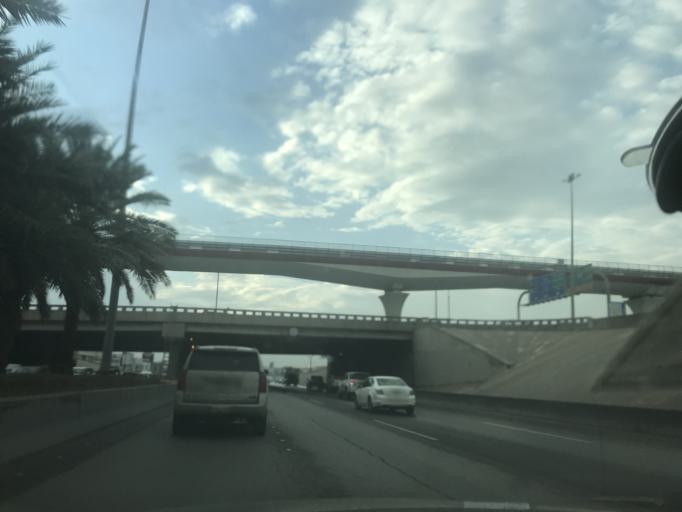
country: SA
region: Ar Riyad
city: Riyadh
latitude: 24.7608
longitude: 46.7386
